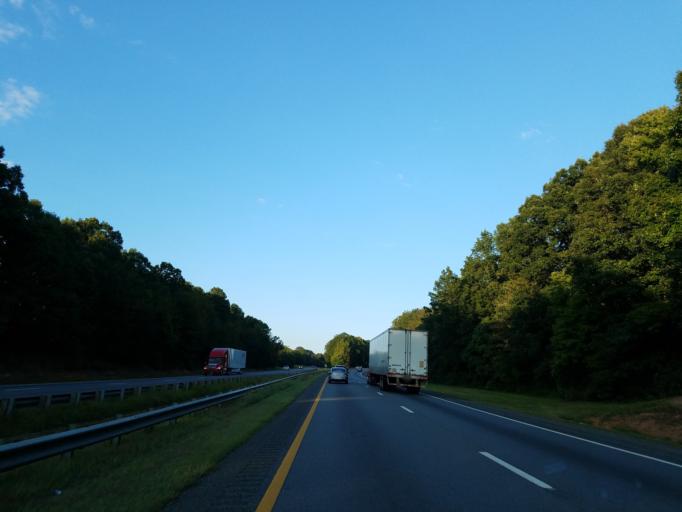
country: US
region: North Carolina
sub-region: Cleveland County
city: White Plains
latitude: 35.1910
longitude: -81.3987
